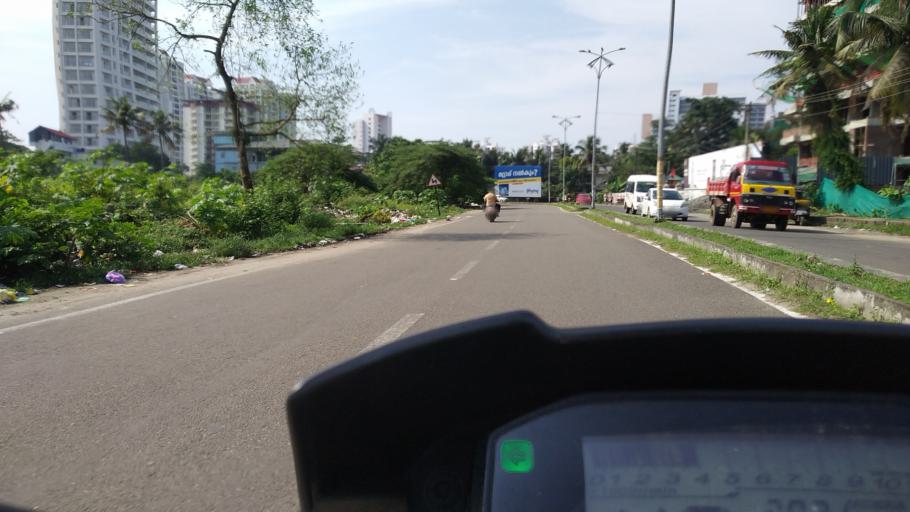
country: IN
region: Kerala
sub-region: Ernakulam
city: Cochin
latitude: 9.9848
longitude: 76.3038
